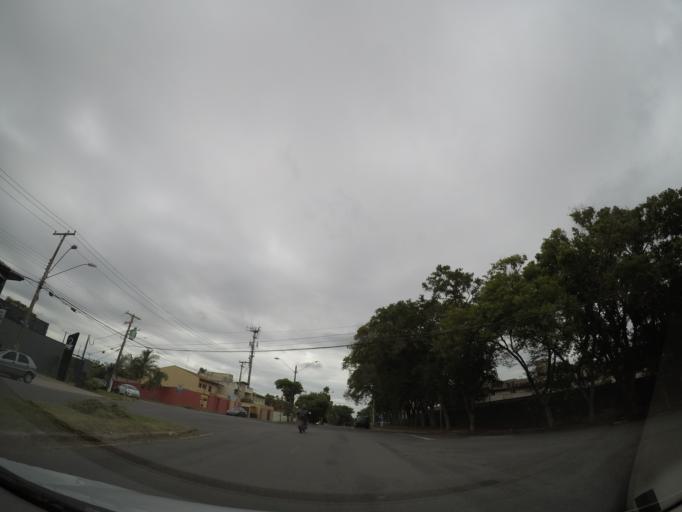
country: BR
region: Sao Paulo
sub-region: Campinas
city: Campinas
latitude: -22.9084
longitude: -47.0363
